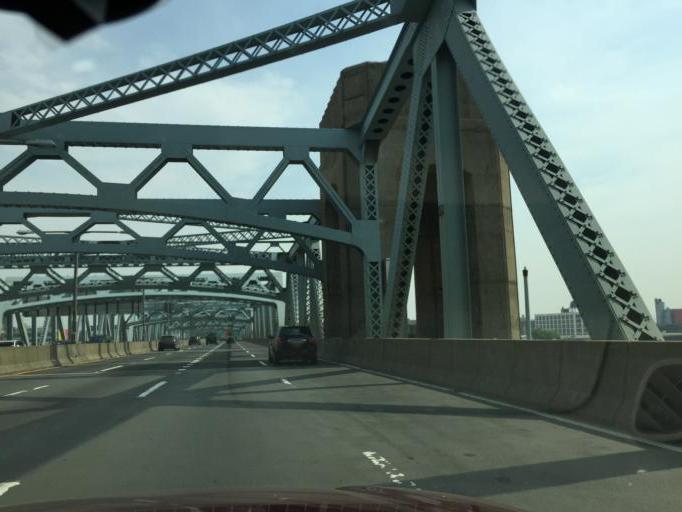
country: US
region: New York
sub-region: New York County
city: Manhattan
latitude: 40.7988
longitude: -73.9190
